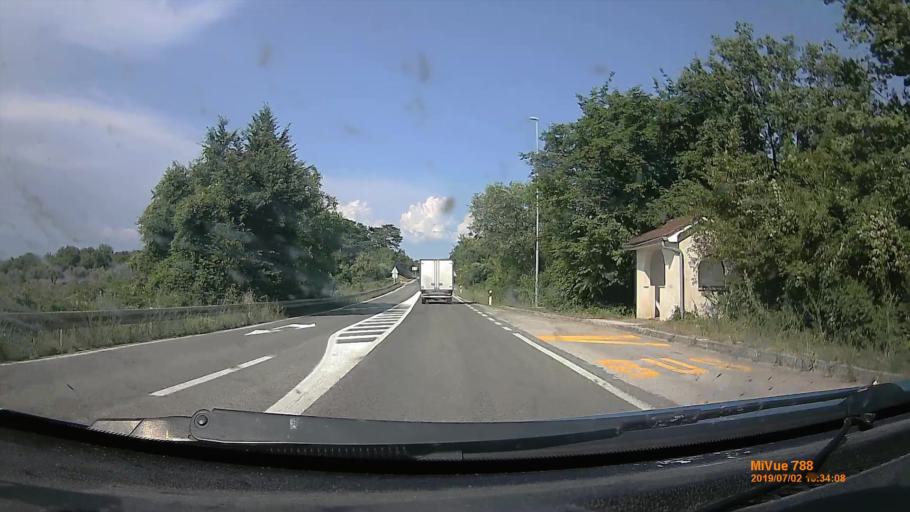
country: HR
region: Primorsko-Goranska
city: Njivice
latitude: 45.0795
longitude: 14.4985
